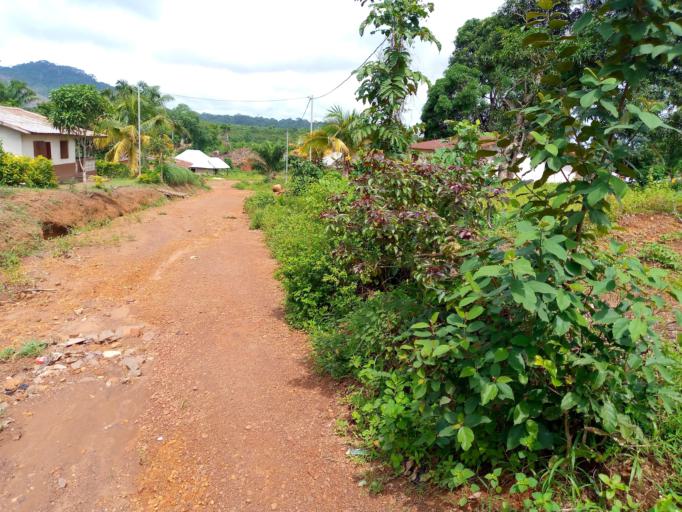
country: SL
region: Southern Province
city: Mogbwemo
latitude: 7.7583
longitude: -12.3096
